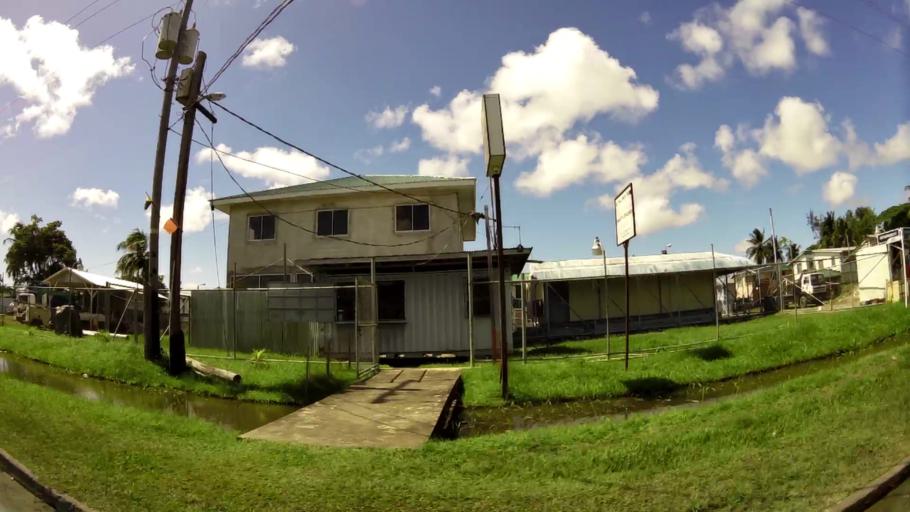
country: GY
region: Demerara-Mahaica
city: Georgetown
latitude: 6.7845
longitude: -58.1334
